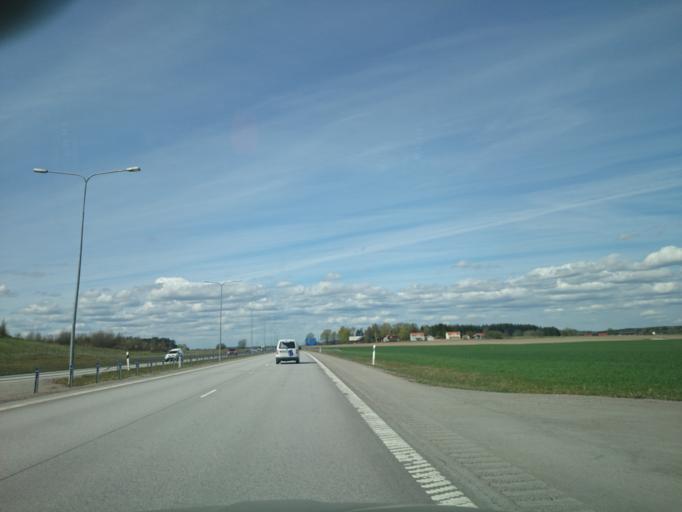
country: SE
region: Uppsala
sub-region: Uppsala Kommun
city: Saevja
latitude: 59.8745
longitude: 17.6987
